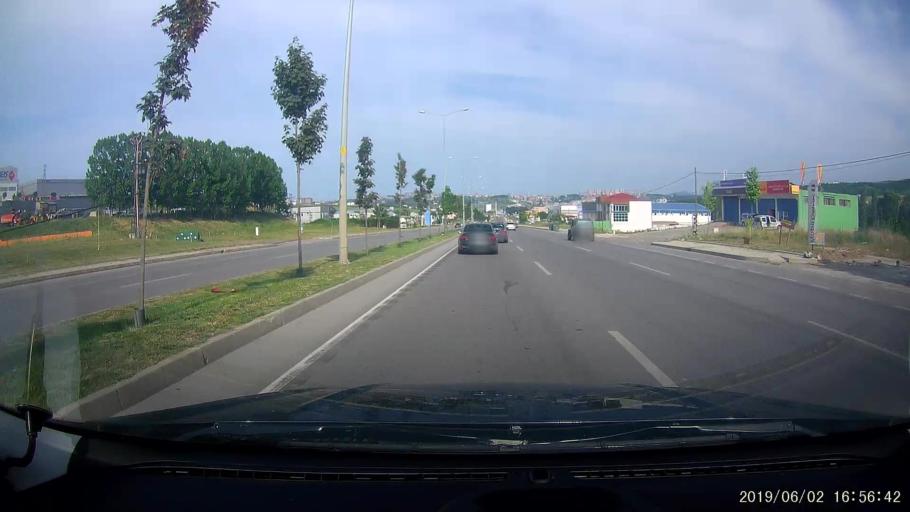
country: TR
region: Samsun
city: Samsun
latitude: 41.2918
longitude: 36.2644
